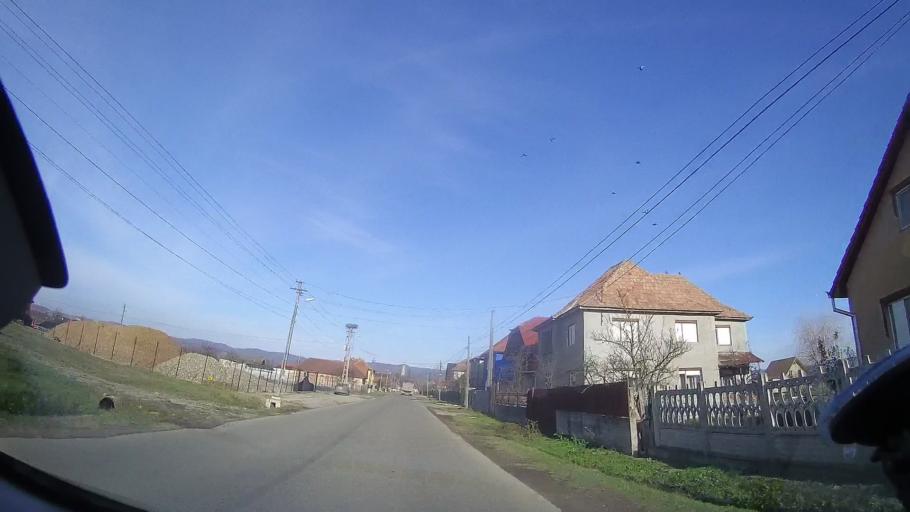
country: RO
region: Bihor
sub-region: Comuna Astileu
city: Astileu
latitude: 47.0334
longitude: 22.3898
